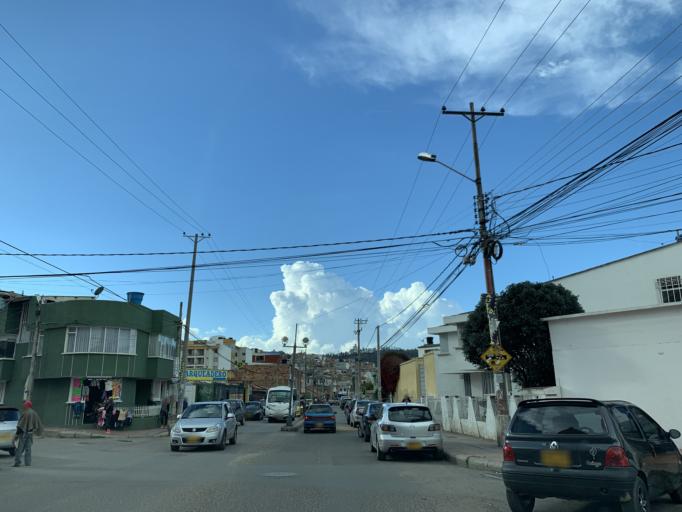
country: CO
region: Boyaca
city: Tunja
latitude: 5.5441
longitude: -73.3595
